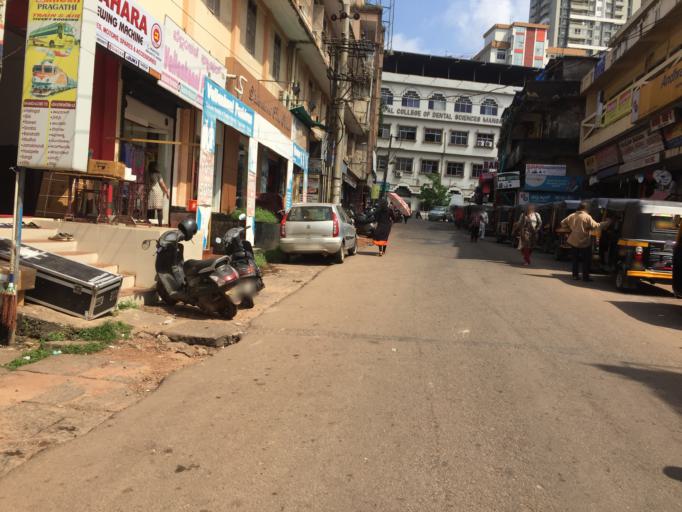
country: IN
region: Karnataka
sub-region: Dakshina Kannada
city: Mangalore
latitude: 12.8687
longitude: 74.8442
